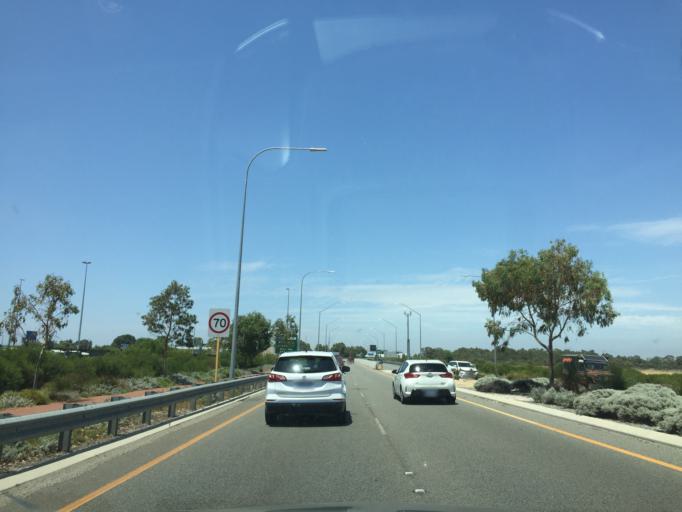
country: AU
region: Western Australia
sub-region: Belmont
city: Kewdale
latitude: -31.9562
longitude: 115.9688
